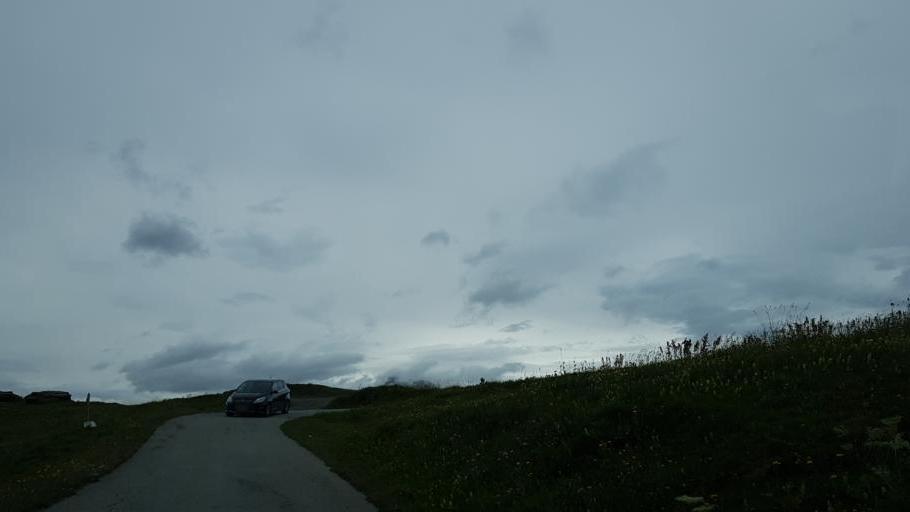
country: IT
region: Piedmont
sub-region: Provincia di Cuneo
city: Serre
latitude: 44.5508
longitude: 7.1192
